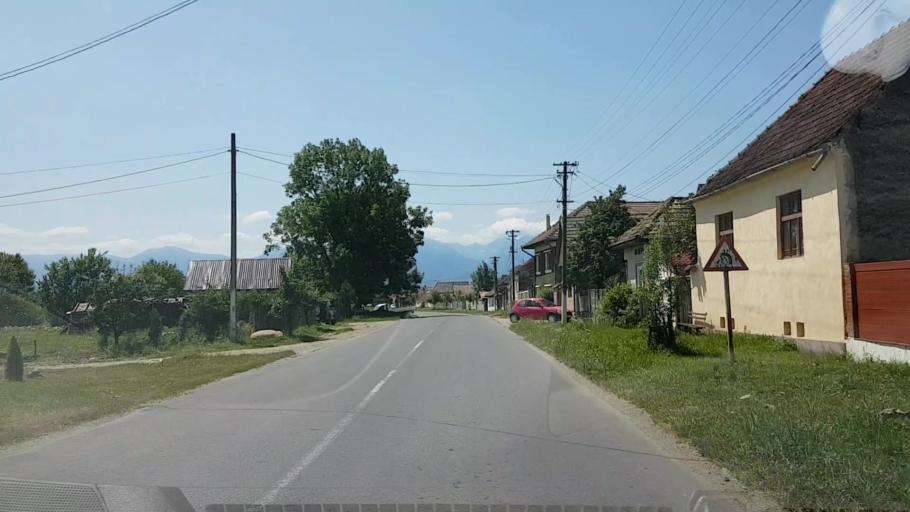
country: RO
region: Brasov
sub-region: Comuna Voila
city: Voila
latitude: 45.8435
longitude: 24.8328
